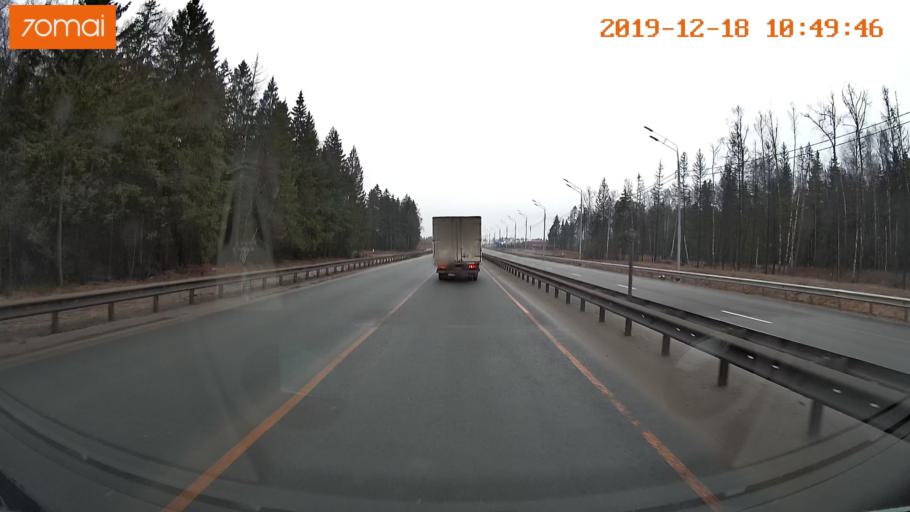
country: RU
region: Moskovskaya
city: Selyatino
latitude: 55.5049
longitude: 37.0139
